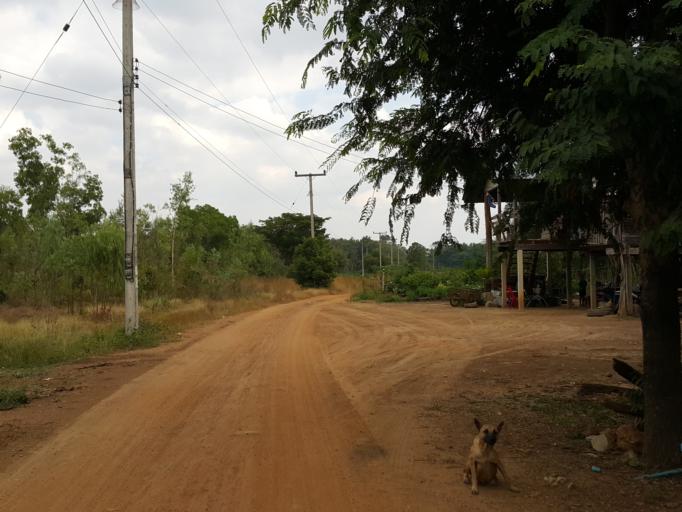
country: TH
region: Sukhothai
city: Thung Saliam
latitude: 17.3904
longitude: 99.5786
